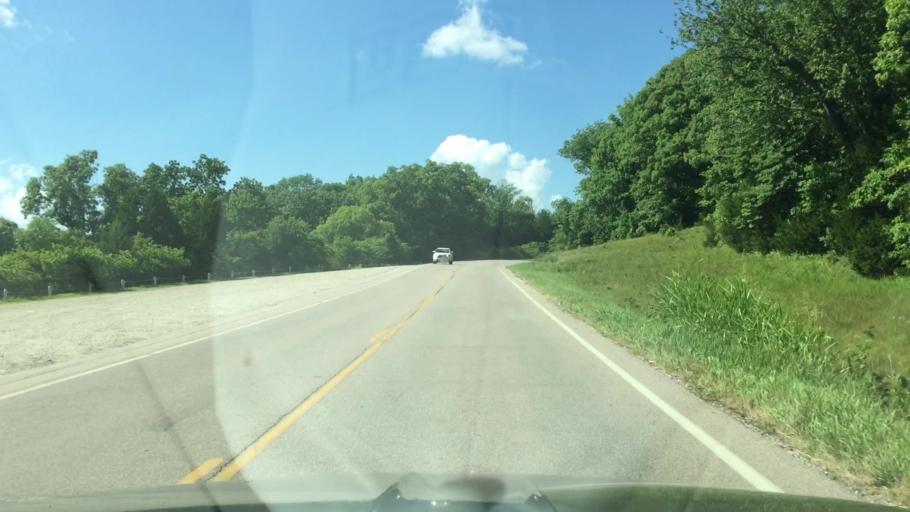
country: US
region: Missouri
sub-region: Miller County
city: Lake Ozark
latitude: 38.2083
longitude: -92.6229
